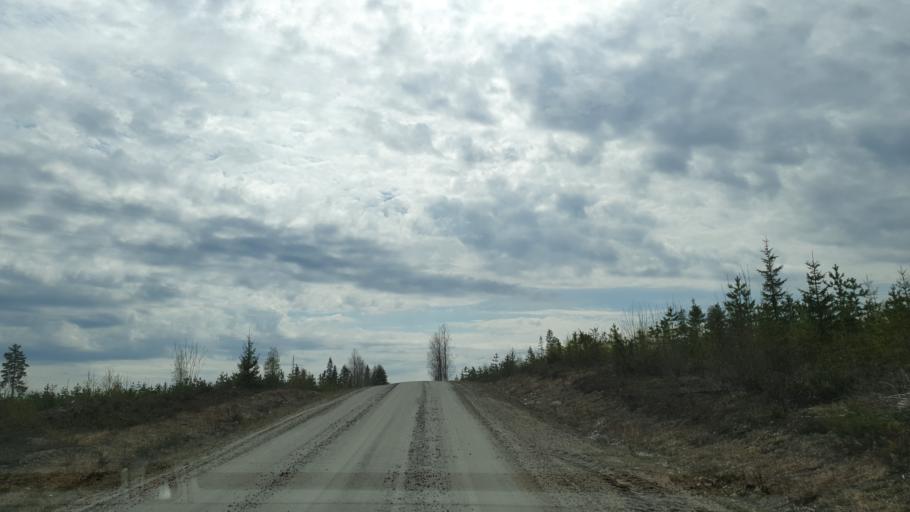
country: FI
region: Kainuu
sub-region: Kehys-Kainuu
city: Kuhmo
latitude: 64.1097
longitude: 29.9561
